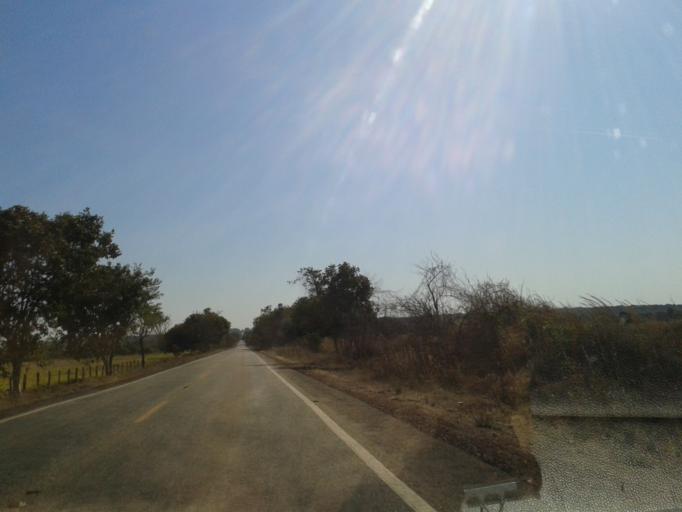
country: BR
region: Goias
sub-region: Mozarlandia
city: Mozarlandia
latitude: -14.5895
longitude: -50.5075
